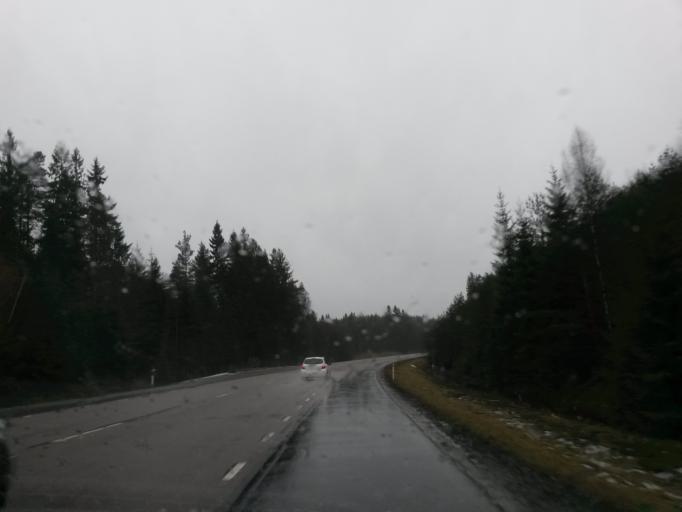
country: SE
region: Vaestra Goetaland
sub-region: Boras Kommun
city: Boras
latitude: 57.6467
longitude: 12.9161
